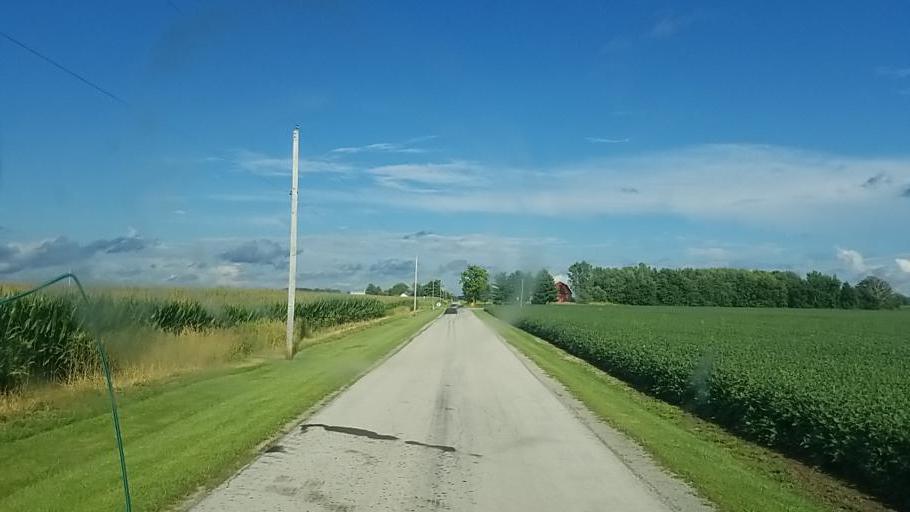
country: US
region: Ohio
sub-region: Wyandot County
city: Upper Sandusky
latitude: 40.7593
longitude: -83.3549
